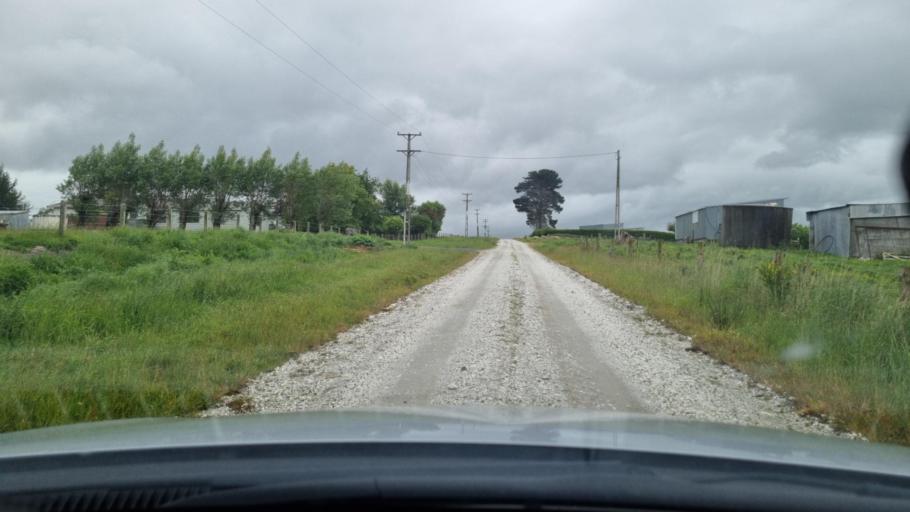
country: NZ
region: Southland
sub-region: Invercargill City
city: Invercargill
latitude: -46.4540
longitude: 168.3939
